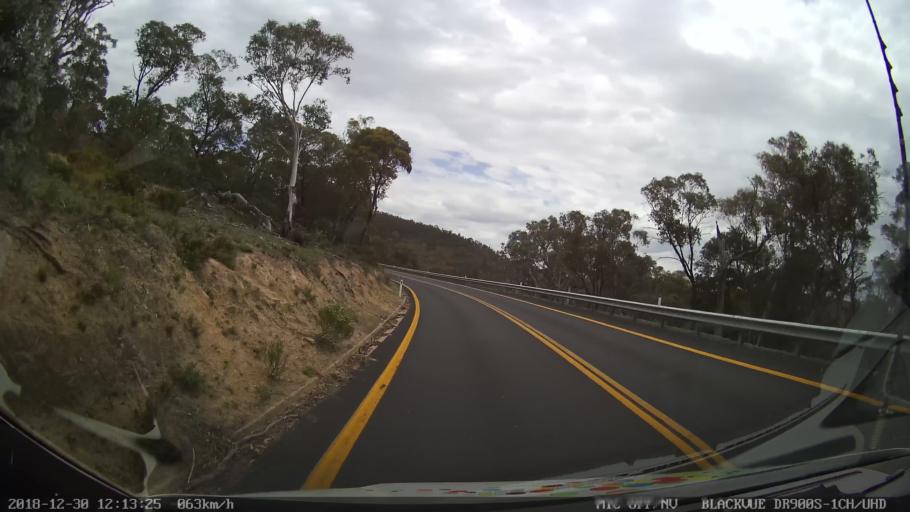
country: AU
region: New South Wales
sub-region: Snowy River
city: Jindabyne
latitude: -36.3487
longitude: 148.5854
